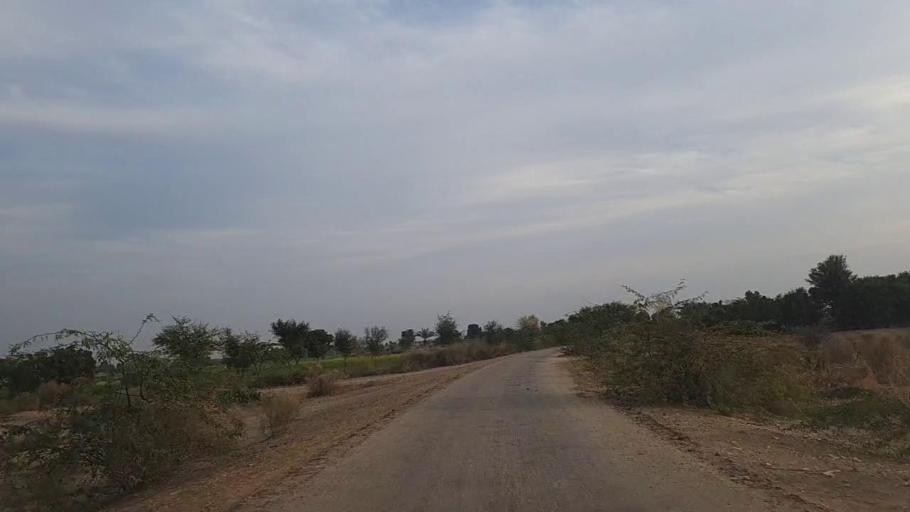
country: PK
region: Sindh
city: Jam Sahib
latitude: 26.4780
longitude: 68.5641
